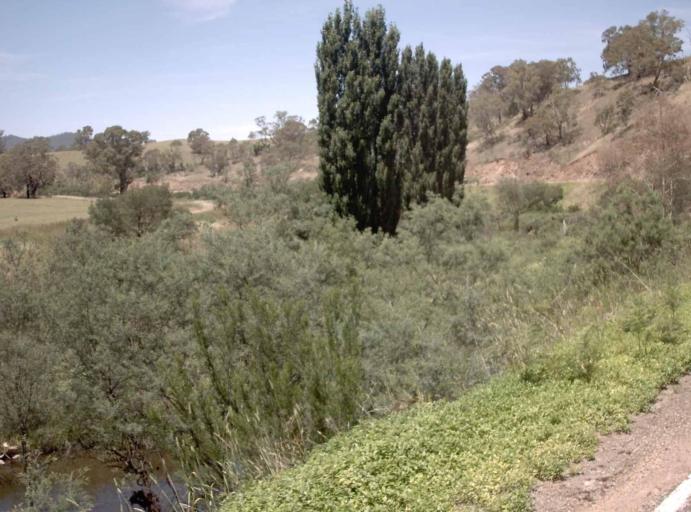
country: AU
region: Victoria
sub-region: East Gippsland
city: Bairnsdale
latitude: -37.3864
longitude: 147.8284
